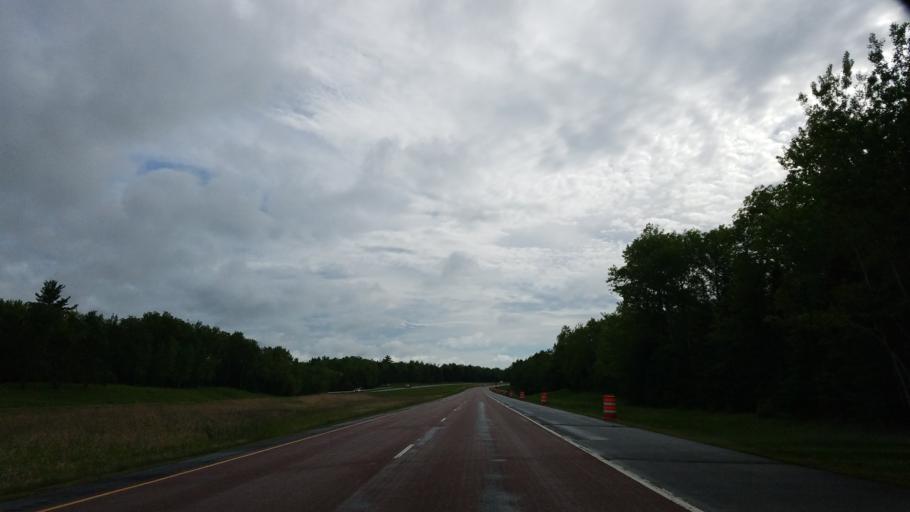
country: US
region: Minnesota
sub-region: Lake County
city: Two Harbors
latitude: 46.9244
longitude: -91.8580
